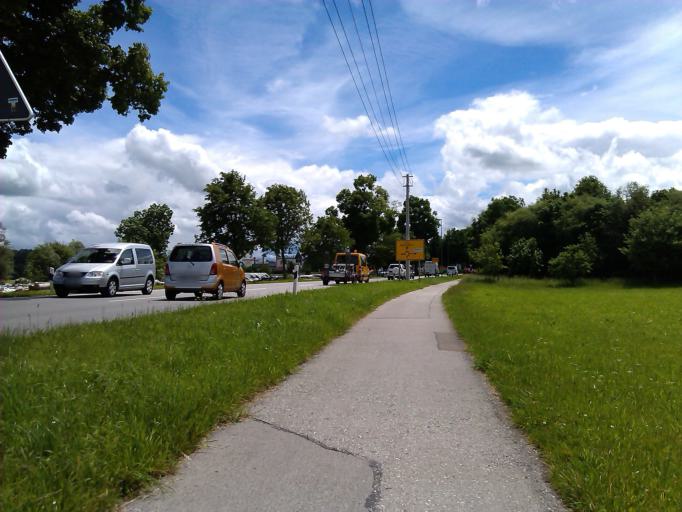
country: DE
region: Bavaria
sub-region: Swabia
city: Biessenhofen
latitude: 47.8394
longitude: 10.6401
